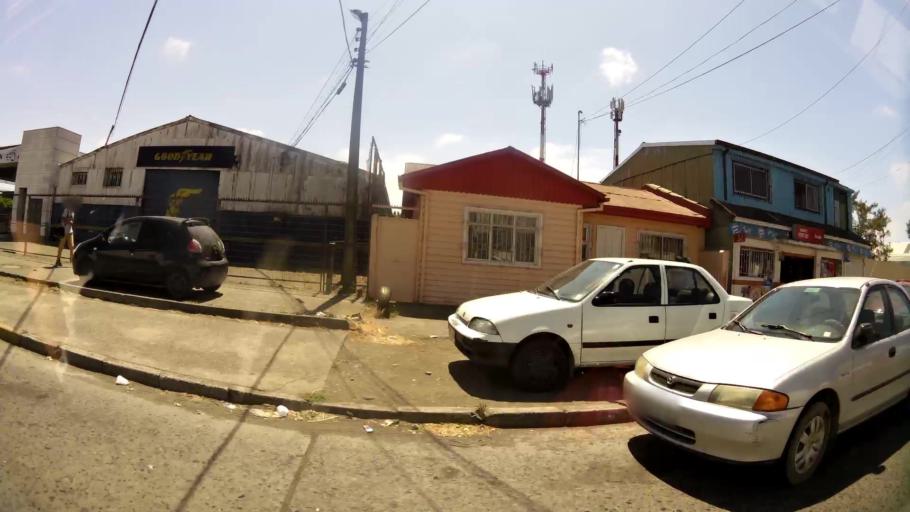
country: CL
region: Biobio
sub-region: Provincia de Concepcion
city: Concepcion
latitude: -36.8065
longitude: -73.0522
